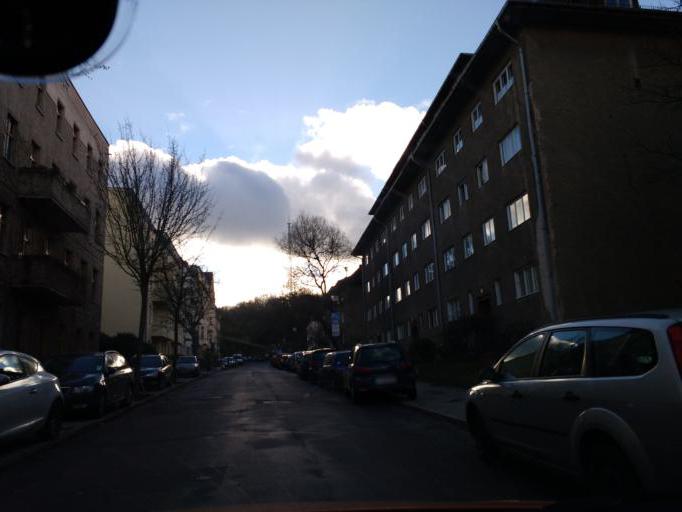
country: DE
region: Brandenburg
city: Potsdam
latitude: 52.3878
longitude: 13.0655
